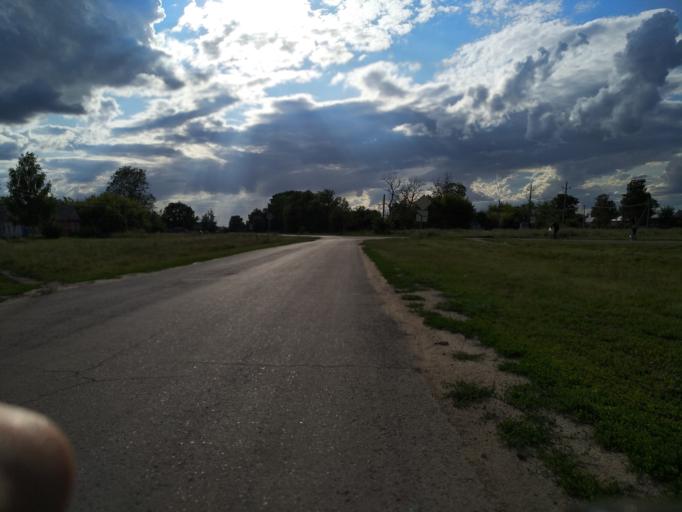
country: RU
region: Lipetsk
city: Dobrinka
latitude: 52.0387
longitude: 40.5413
